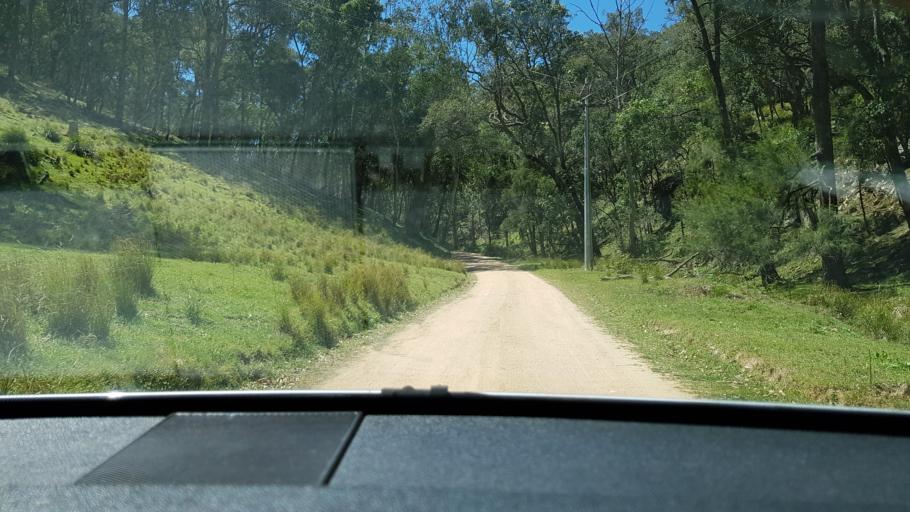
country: AU
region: New South Wales
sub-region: Blue Mountains Municipality
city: Katoomba
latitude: -33.7781
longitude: 150.2335
